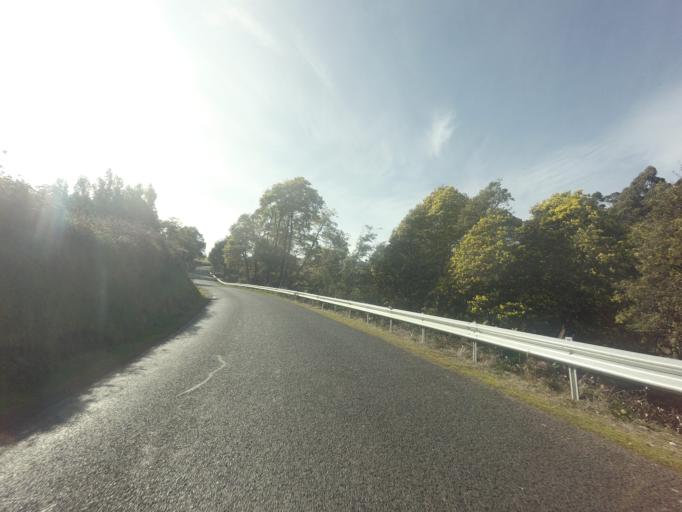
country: AU
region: Tasmania
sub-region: Kingborough
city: Kettering
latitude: -43.1727
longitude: 147.1669
